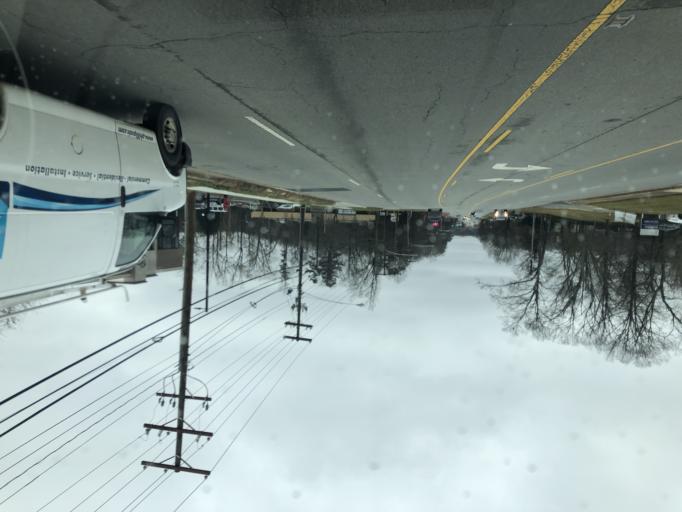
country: US
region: North Carolina
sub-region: Gaston County
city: Ranlo
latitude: 35.2757
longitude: -81.1354
